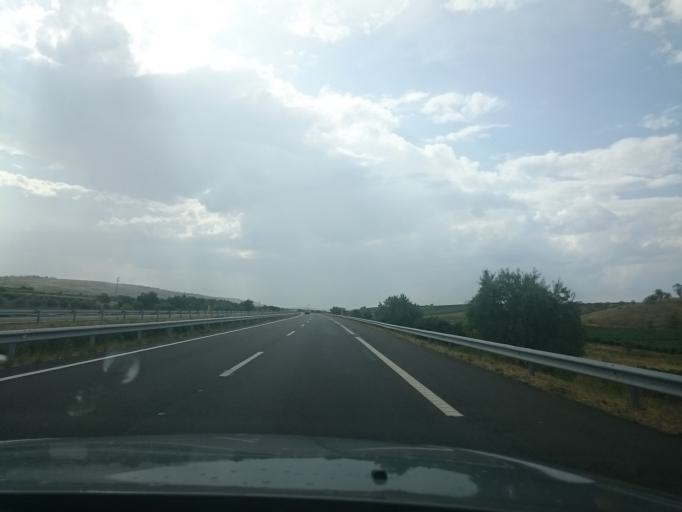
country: ES
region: Navarre
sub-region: Provincia de Navarra
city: Sartaguda
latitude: 42.3766
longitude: -2.0929
